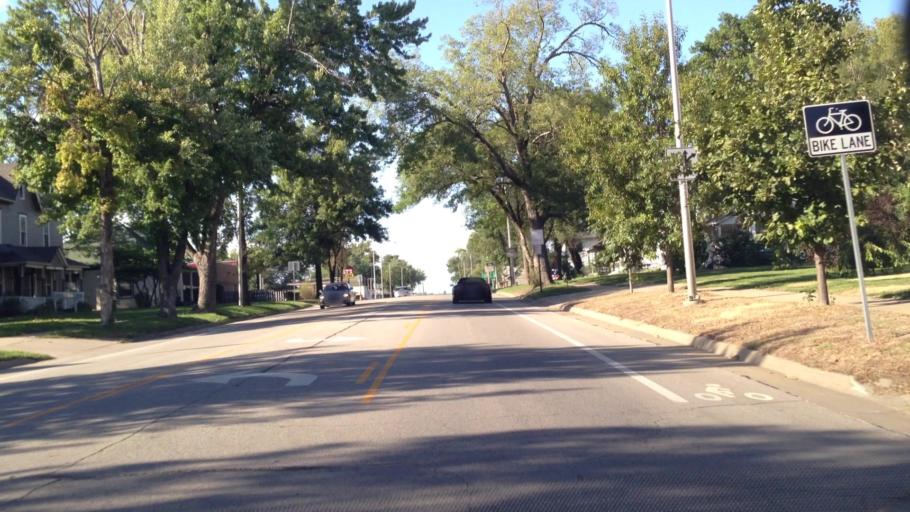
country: US
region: Kansas
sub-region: Franklin County
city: Ottawa
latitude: 38.6289
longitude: -95.2677
